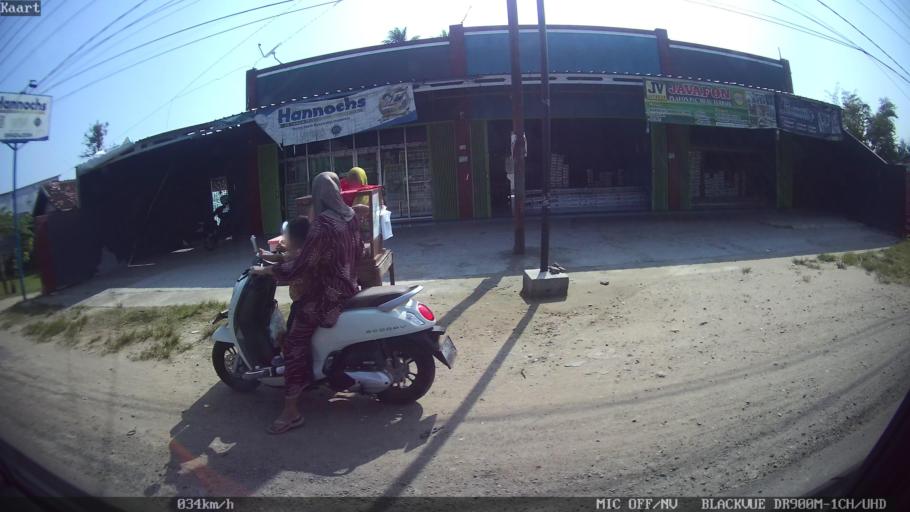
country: ID
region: Lampung
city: Natar
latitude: -5.2522
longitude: 105.1826
